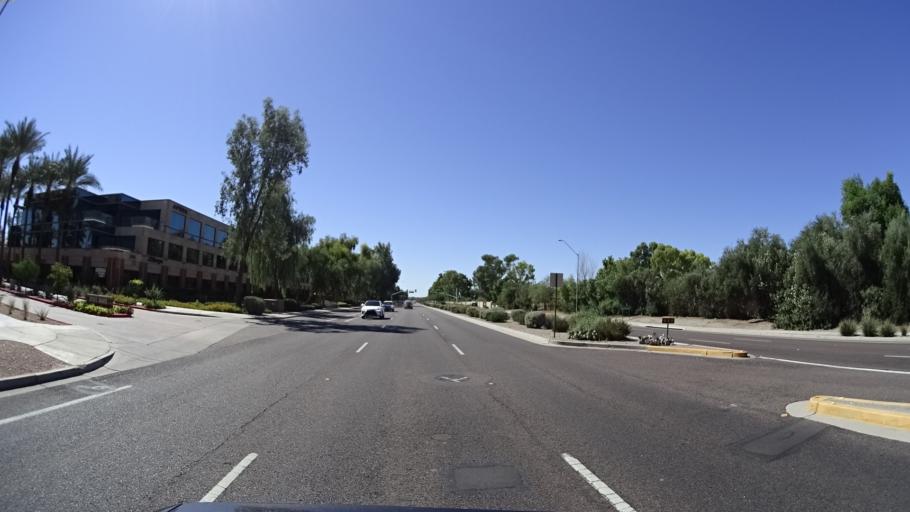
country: US
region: Arizona
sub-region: Maricopa County
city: Paradise Valley
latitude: 33.5620
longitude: -111.9260
